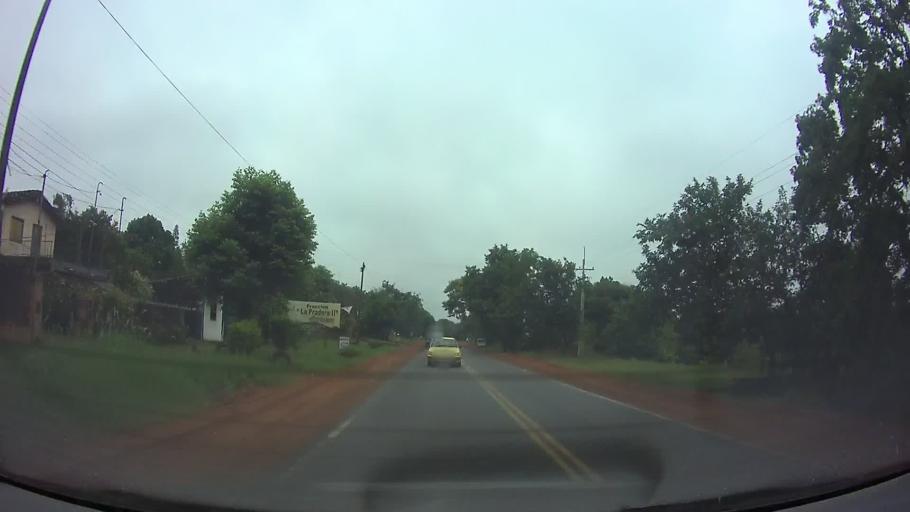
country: PY
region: Central
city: Itaugua
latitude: -25.4235
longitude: -57.3635
